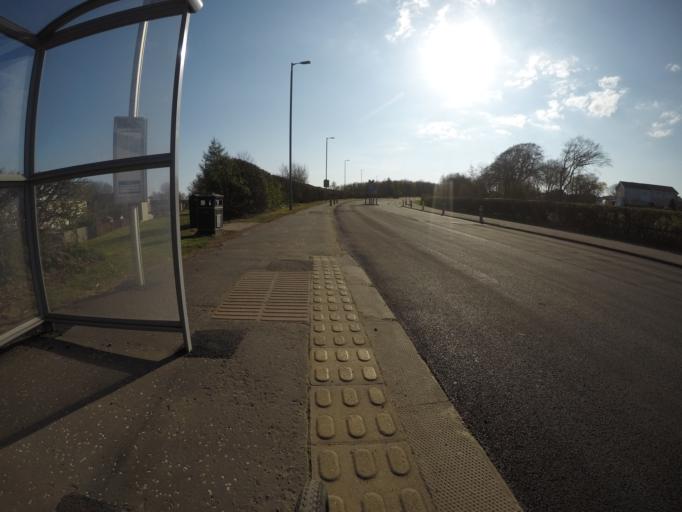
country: GB
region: Scotland
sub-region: North Ayrshire
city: Kilwinning
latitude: 55.6511
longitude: -4.7196
